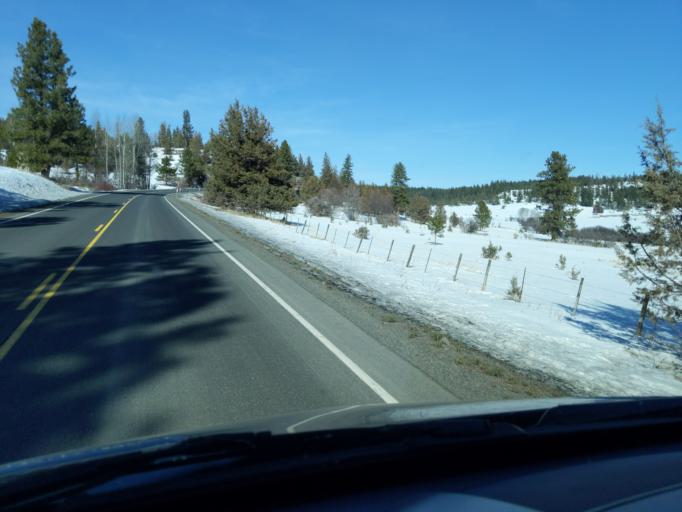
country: US
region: Oregon
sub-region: Grant County
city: John Day
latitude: 44.9018
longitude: -119.0134
